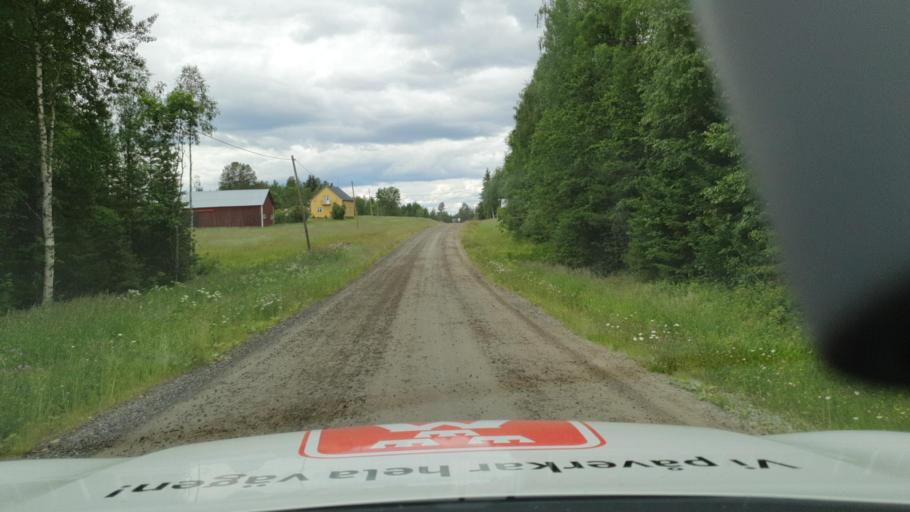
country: SE
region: Vaesterbotten
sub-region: Bjurholms Kommun
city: Bjurholm
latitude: 63.7925
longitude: 19.0991
